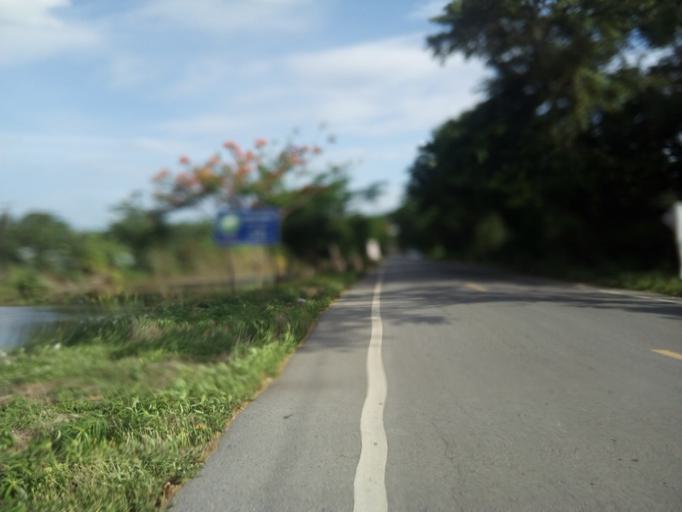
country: TH
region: Pathum Thani
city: Nong Suea
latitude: 14.1327
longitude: 100.8460
